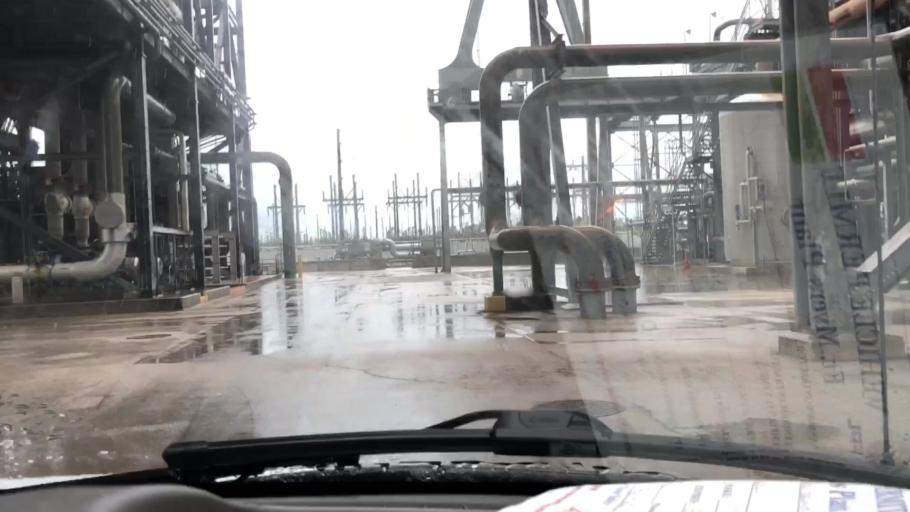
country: US
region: Florida
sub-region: Lee County
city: Tice
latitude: 26.6976
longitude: -81.7837
